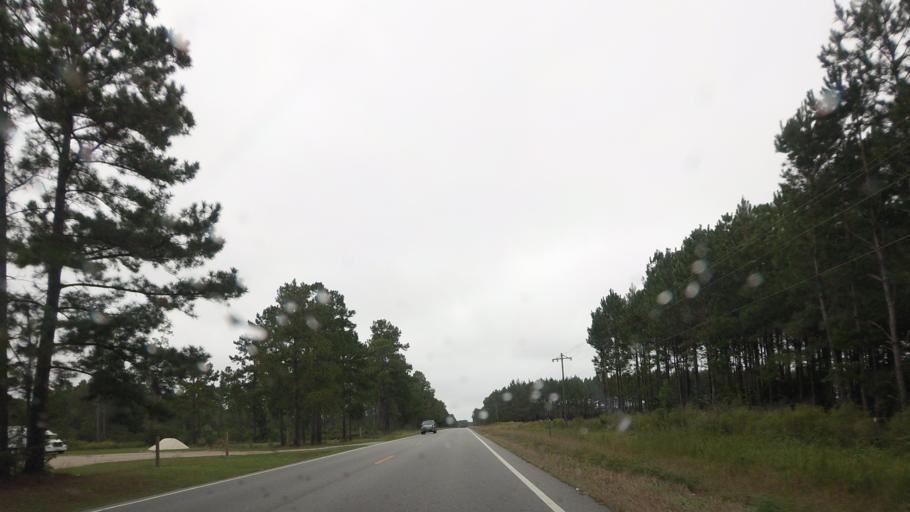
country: US
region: Georgia
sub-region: Berrien County
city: Nashville
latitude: 31.2736
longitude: -83.2396
